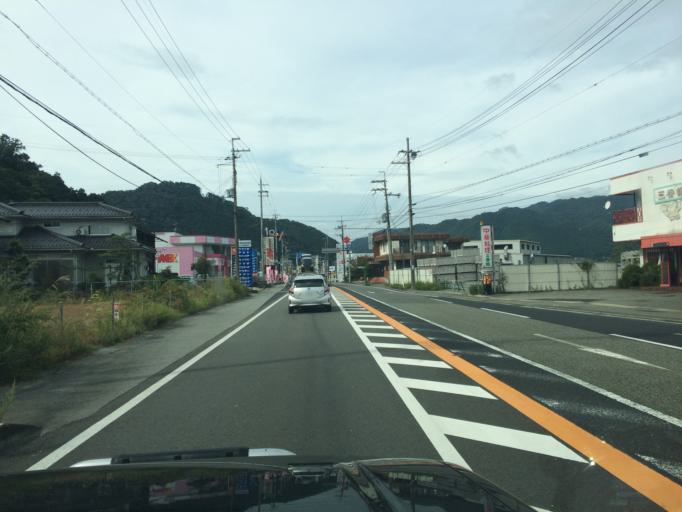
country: JP
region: Hyogo
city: Toyooka
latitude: 35.3439
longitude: 134.8406
